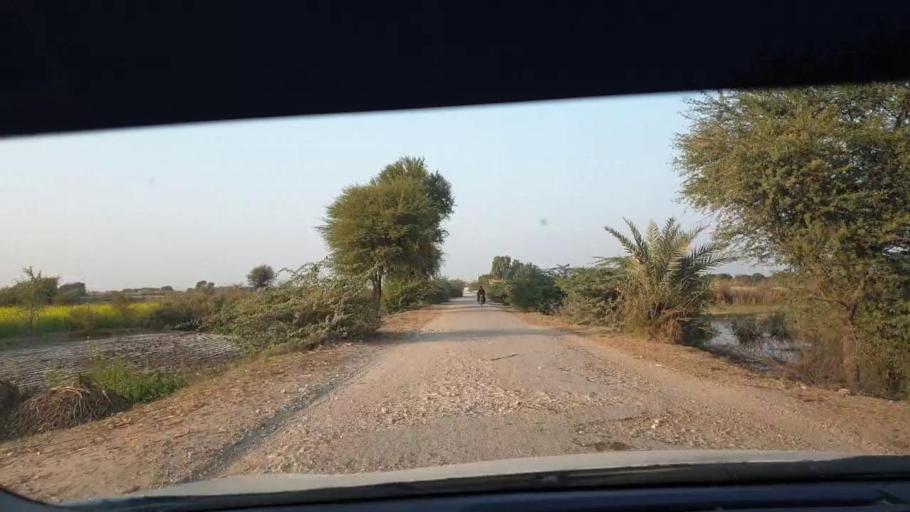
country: PK
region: Sindh
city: Berani
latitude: 25.8573
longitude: 68.8164
